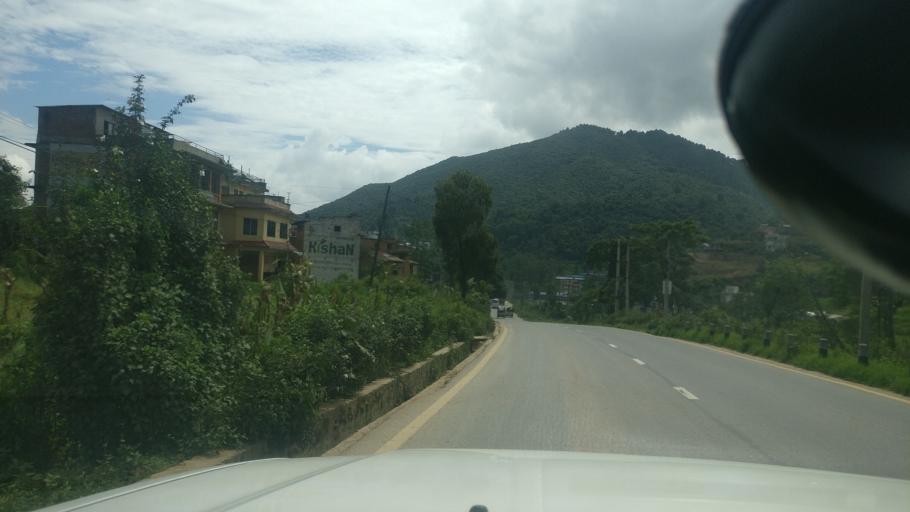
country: NP
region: Central Region
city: Banepa
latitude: 27.6338
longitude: 85.4920
